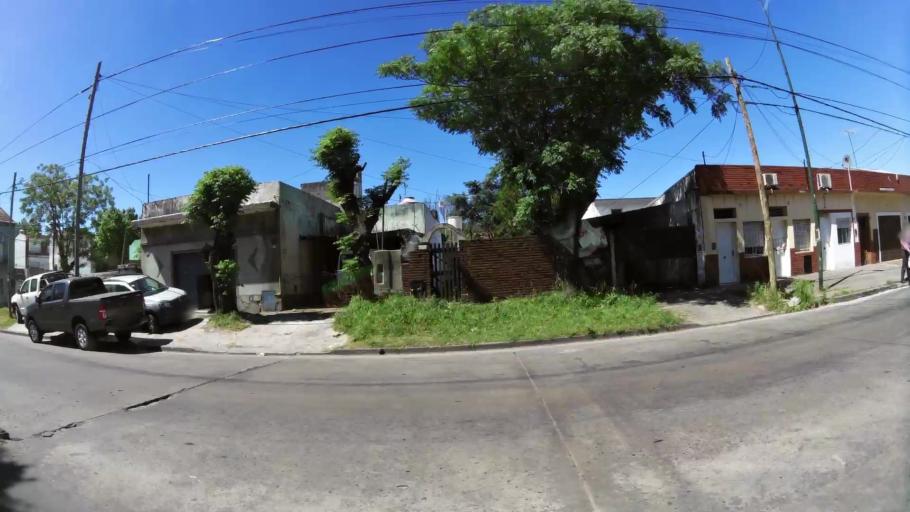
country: AR
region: Buenos Aires
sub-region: Partido de General San Martin
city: General San Martin
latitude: -34.5234
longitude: -58.5616
